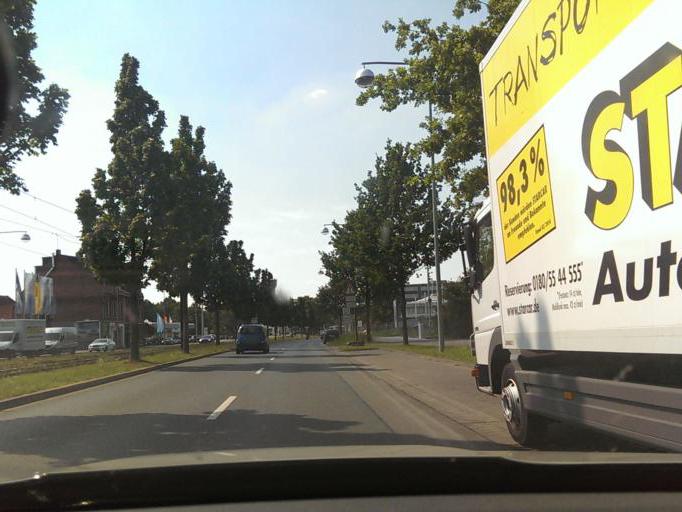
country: DE
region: Lower Saxony
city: Hannover
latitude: 52.4046
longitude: 9.7957
